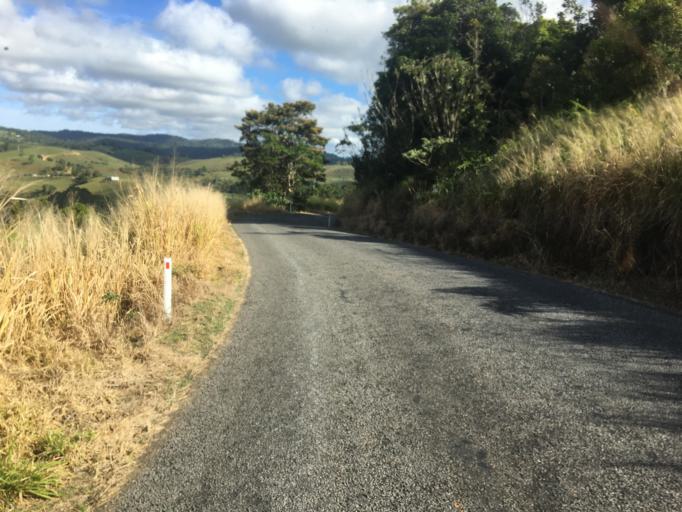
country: AU
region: Queensland
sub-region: Tablelands
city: Ravenshoe
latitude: -17.5365
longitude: 145.6102
